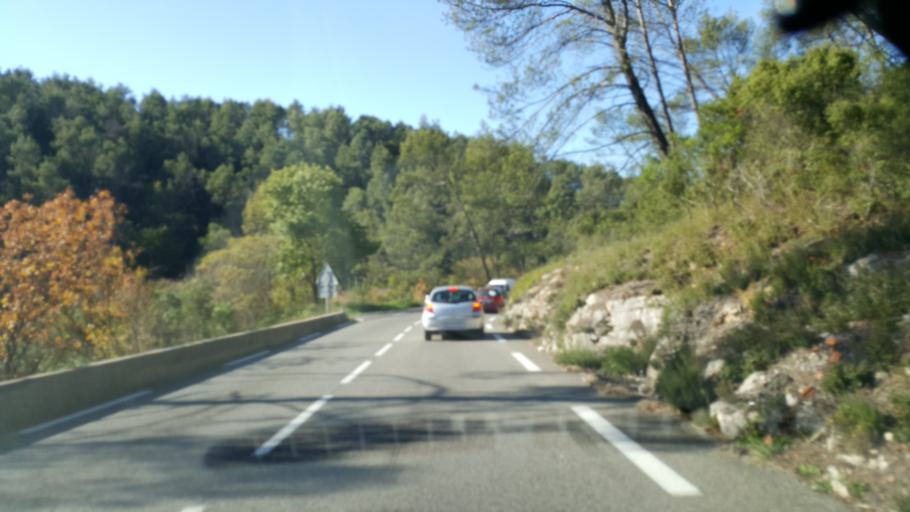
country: FR
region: Provence-Alpes-Cote d'Azur
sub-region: Departement du Var
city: Saint-Zacharie
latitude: 43.3824
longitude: 5.7379
